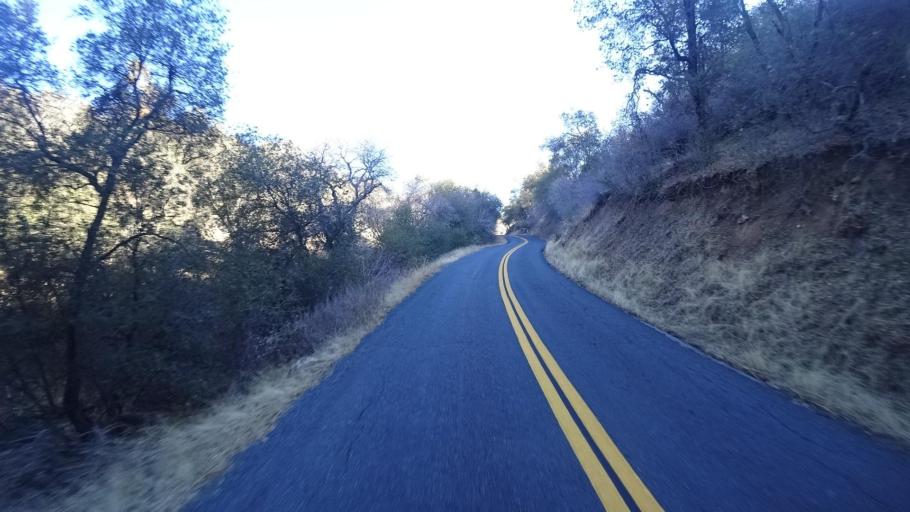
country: US
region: California
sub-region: Kern County
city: Alta Sierra
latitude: 35.7903
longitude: -118.7417
